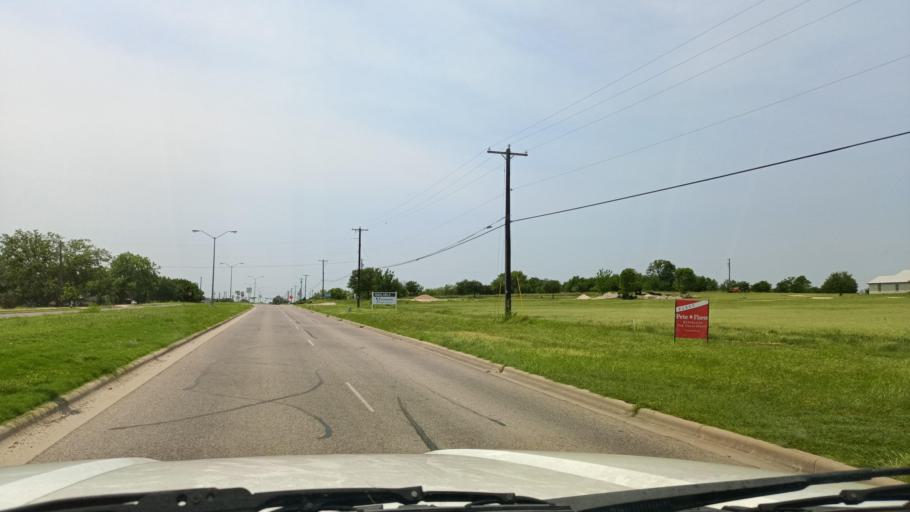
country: US
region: Texas
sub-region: Bell County
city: Morgans Point Resort
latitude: 31.1226
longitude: -97.4144
